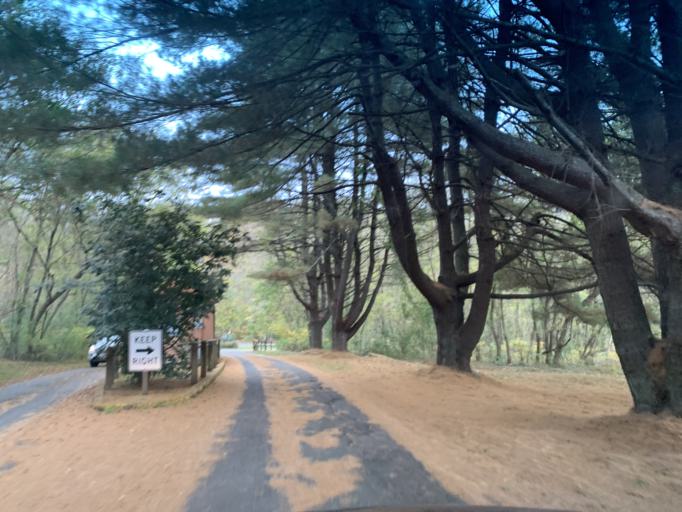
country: US
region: Maryland
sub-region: Harford County
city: Havre de Grace
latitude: 39.6223
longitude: -76.1606
